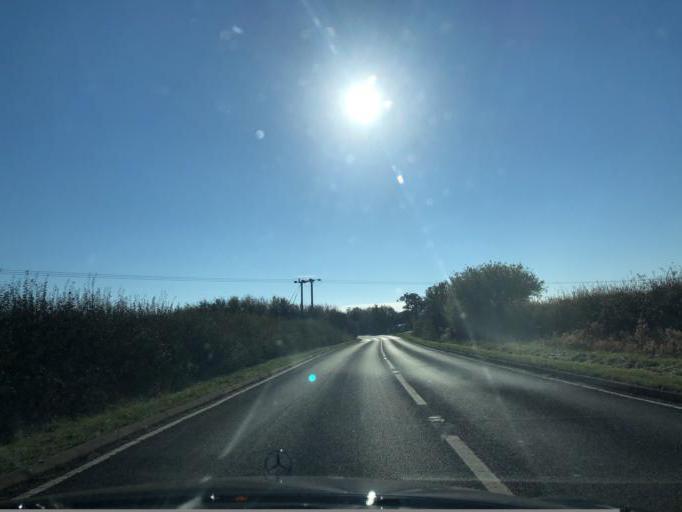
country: GB
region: England
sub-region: Warwickshire
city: Southam
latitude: 52.2355
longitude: -1.3909
